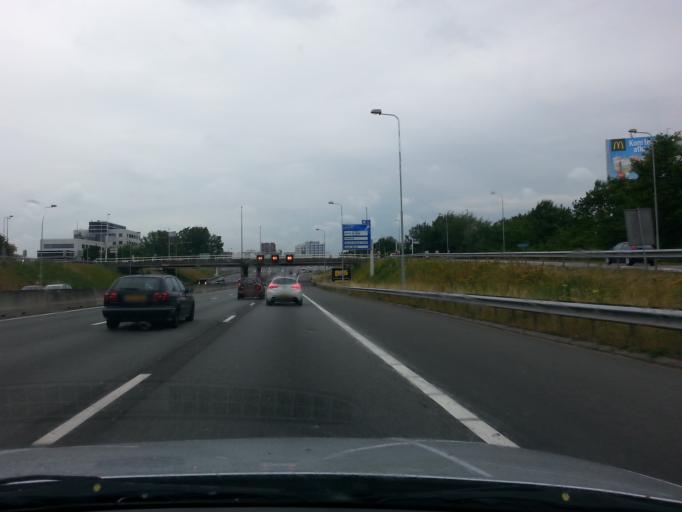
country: NL
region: North Holland
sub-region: Gemeente Amstelveen
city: Amstelveen
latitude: 52.3444
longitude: 4.8412
